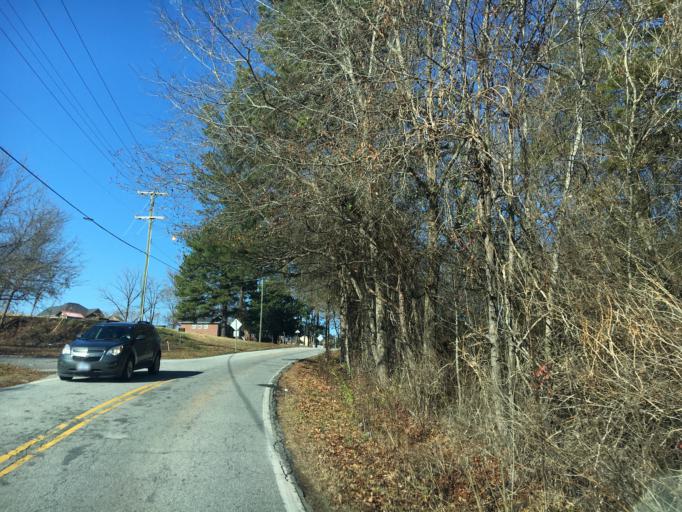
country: US
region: South Carolina
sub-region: Greenville County
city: Greer
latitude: 34.8938
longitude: -82.2512
